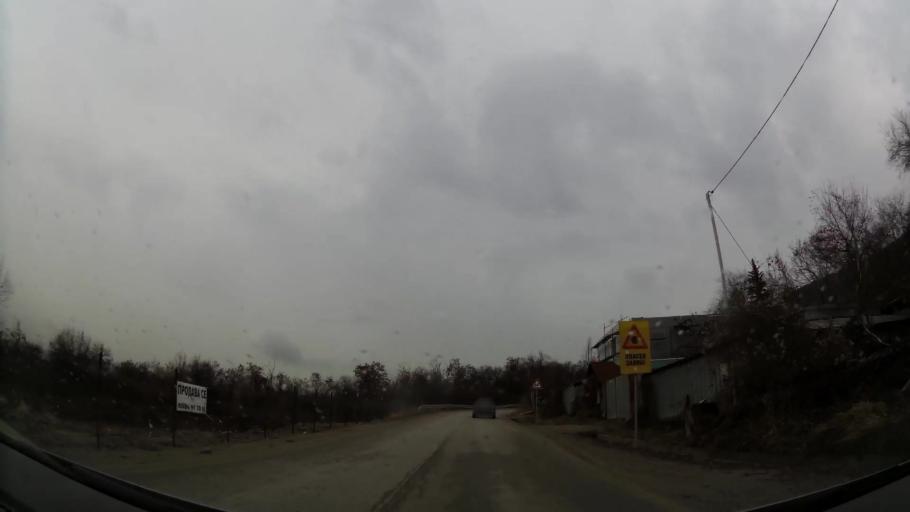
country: BG
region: Sofia-Capital
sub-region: Stolichna Obshtina
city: Sofia
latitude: 42.6062
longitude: 23.3682
